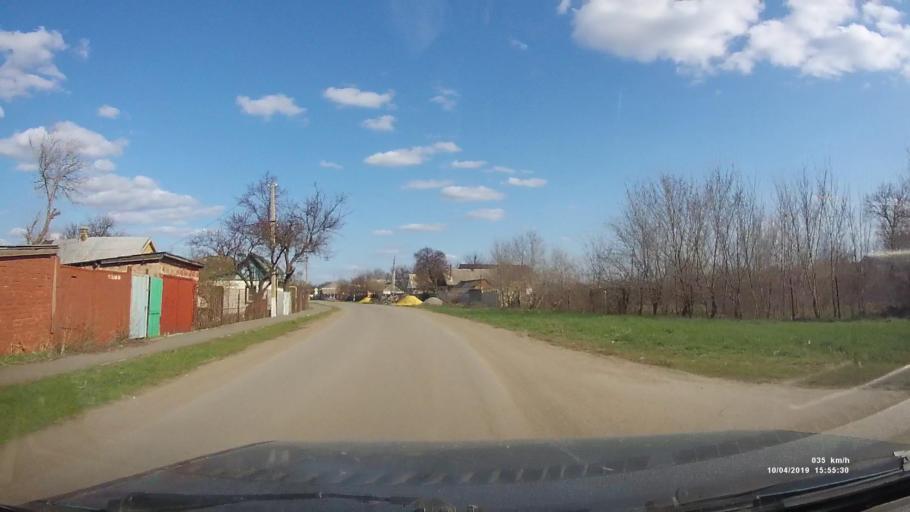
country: RU
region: Rostov
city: Masalovka
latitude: 48.4124
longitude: 40.2654
